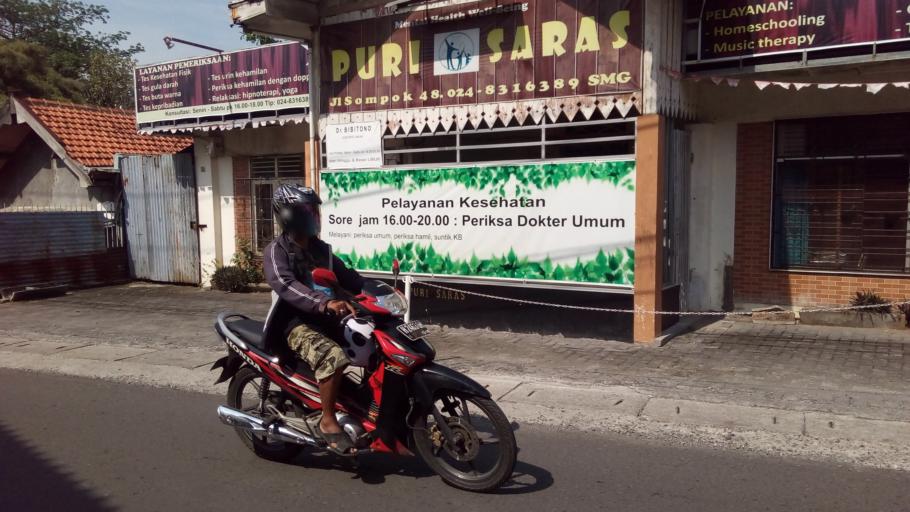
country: ID
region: Central Java
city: Semarang
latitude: -7.0026
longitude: 110.4366
